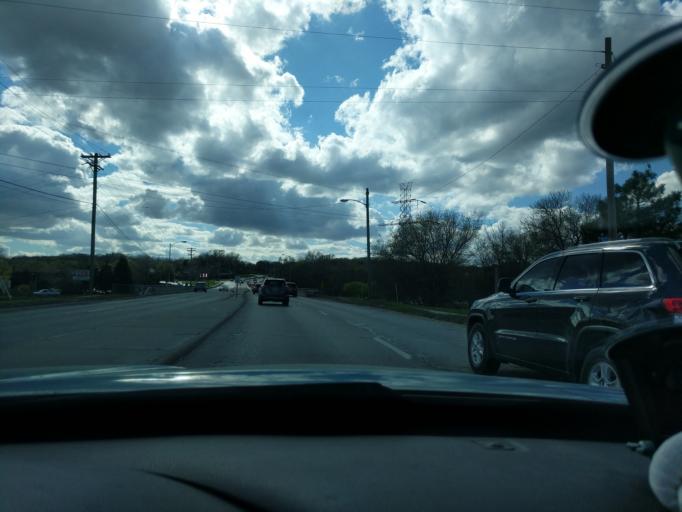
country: US
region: Nebraska
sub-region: Douglas County
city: Ralston
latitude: 41.2342
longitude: -96.0540
